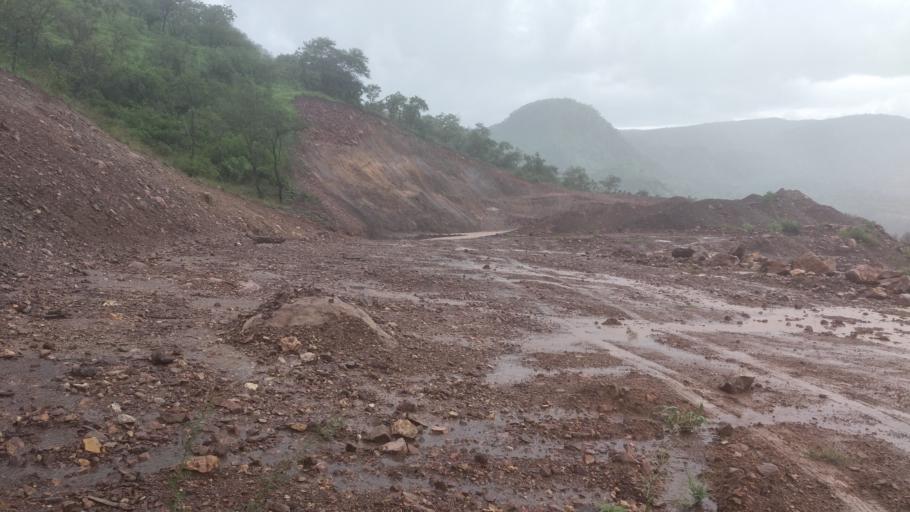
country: ET
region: Southern Nations, Nationalities, and People's Region
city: Areka
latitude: 7.6092
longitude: 37.5118
